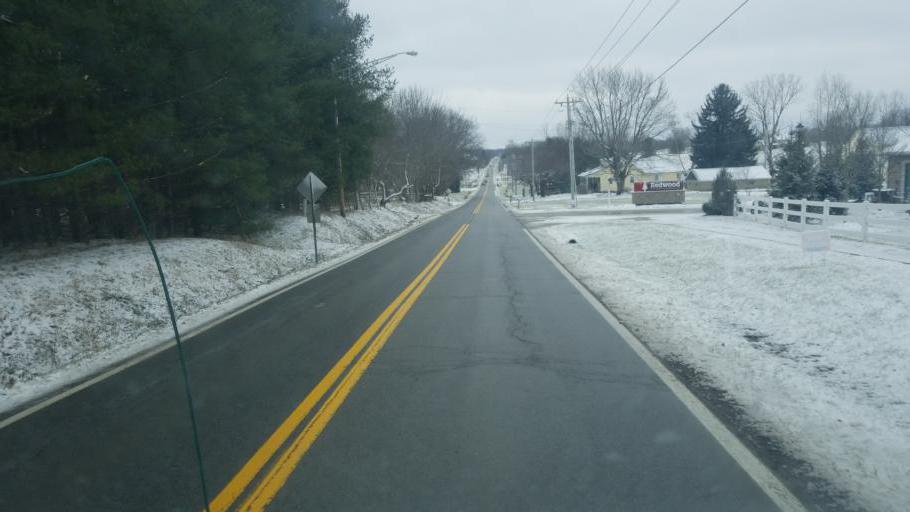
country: US
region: Ohio
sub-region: Licking County
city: Johnstown
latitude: 40.1391
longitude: -82.6954
